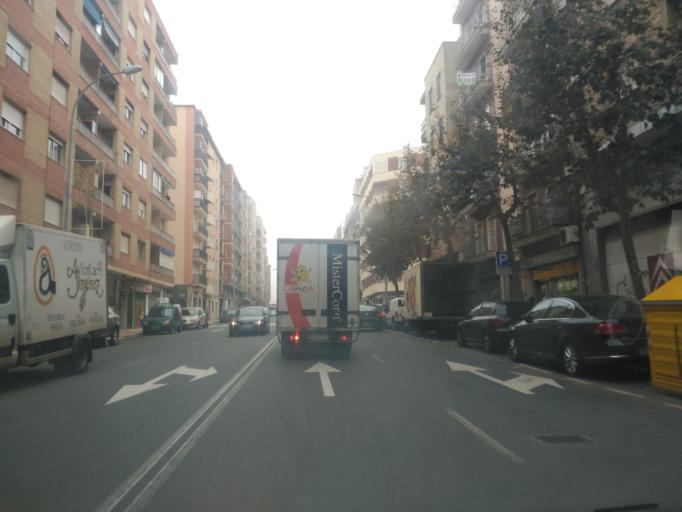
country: ES
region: Castille and Leon
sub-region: Provincia de Salamanca
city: Salamanca
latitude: 40.9686
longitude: -5.6499
